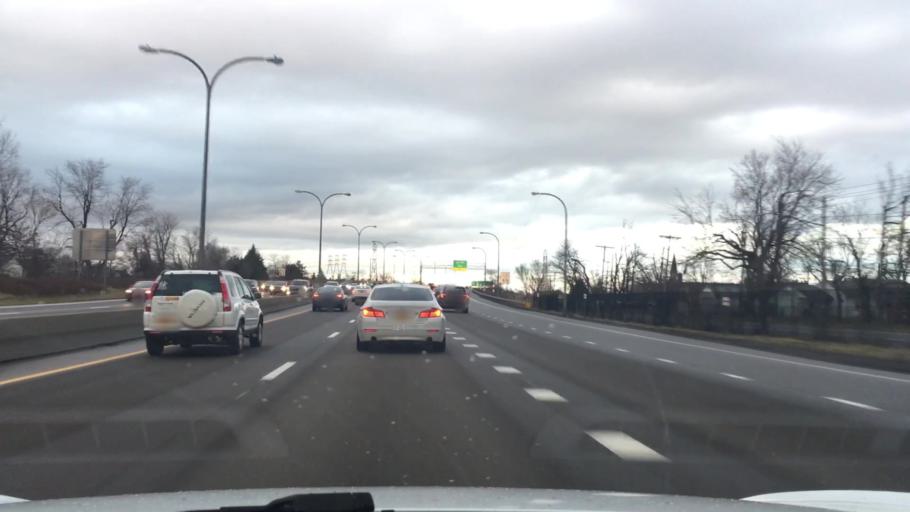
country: US
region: New York
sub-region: Erie County
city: Cheektowaga
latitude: 42.9327
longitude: -78.7765
